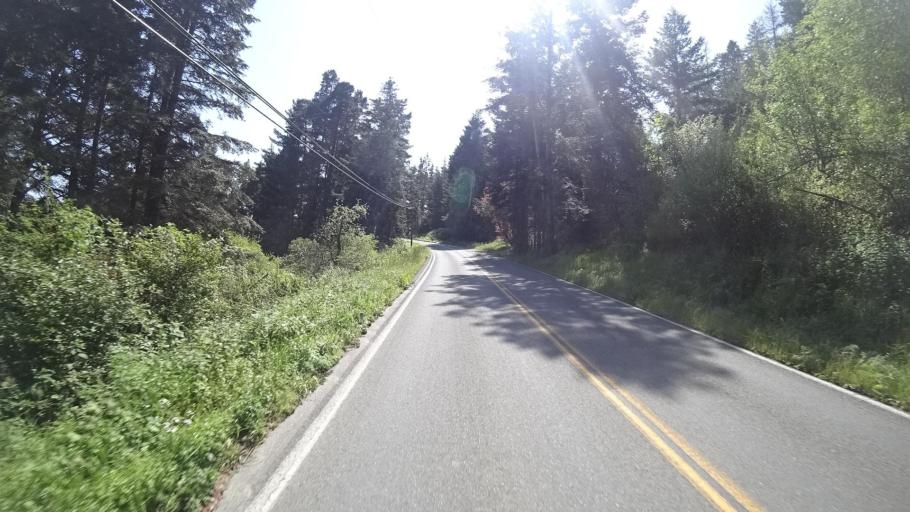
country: US
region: California
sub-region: Humboldt County
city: Hydesville
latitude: 40.5527
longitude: -124.1119
